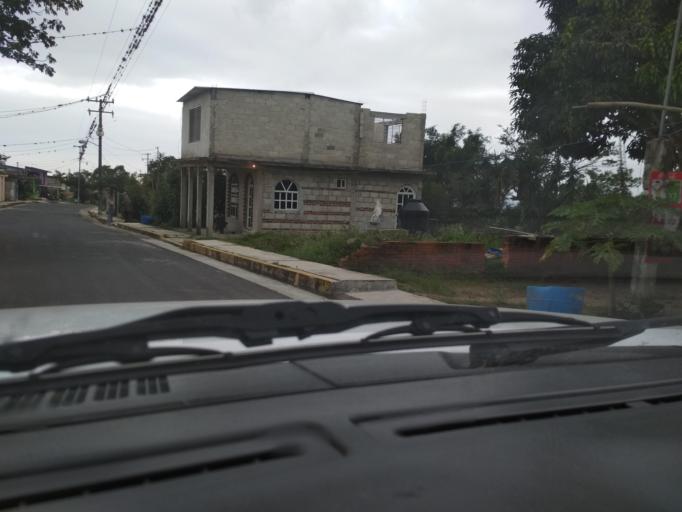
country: MX
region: Veracruz
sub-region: Emiliano Zapata
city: Dos Rios
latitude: 19.5227
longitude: -96.7969
